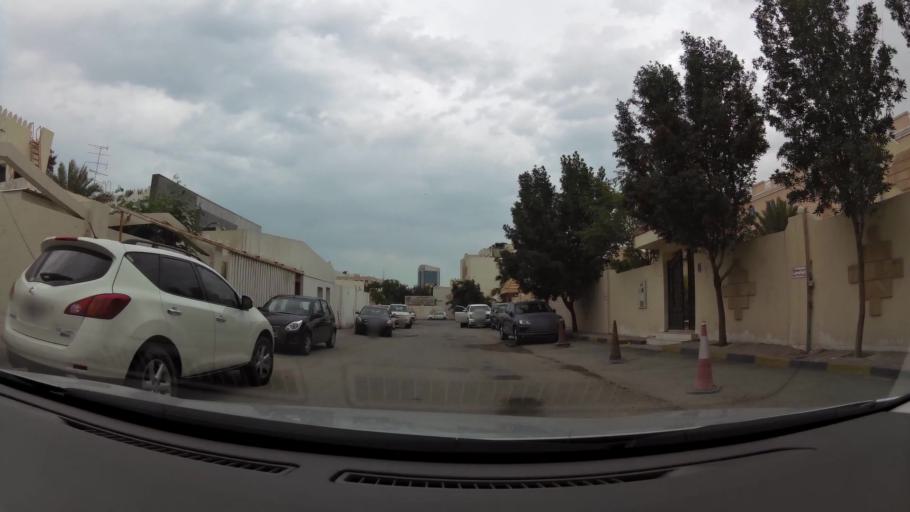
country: QA
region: Baladiyat ad Dawhah
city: Doha
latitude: 25.2744
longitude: 51.5015
